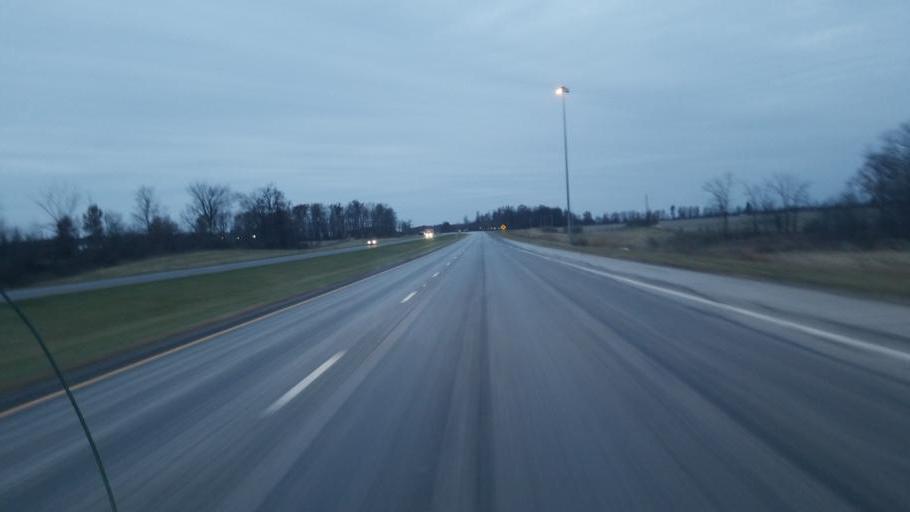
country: US
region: Ohio
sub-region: Hancock County
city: Arlington
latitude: 40.8274
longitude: -83.6628
